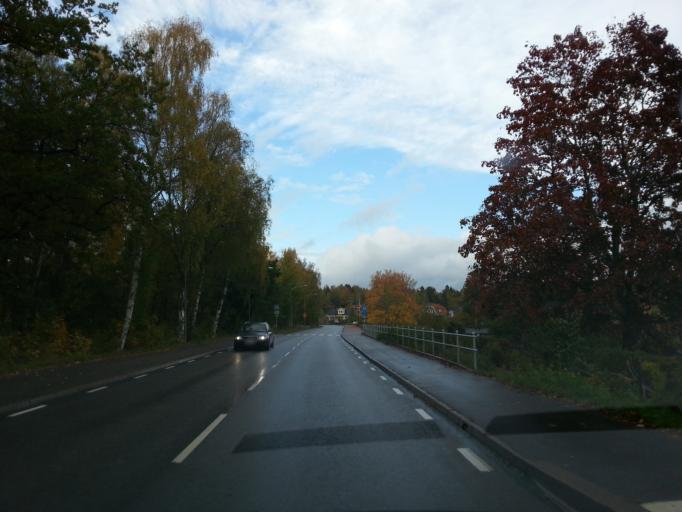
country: SE
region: OEstergoetland
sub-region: Norrkopings Kommun
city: Krokek
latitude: 58.6638
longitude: 16.3717
